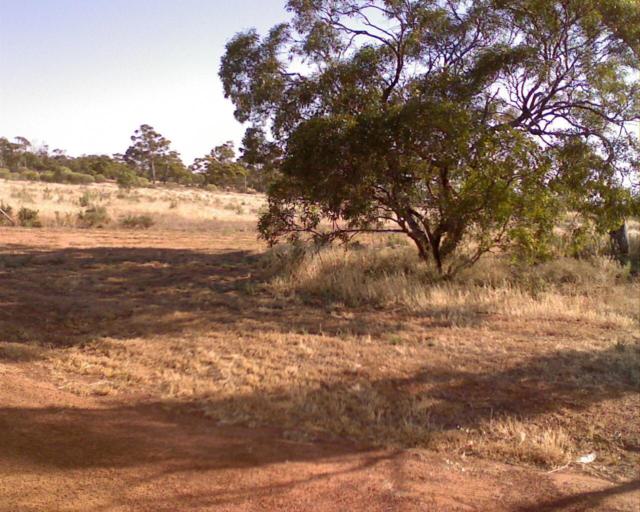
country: AU
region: Western Australia
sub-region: Merredin
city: Merredin
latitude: -31.1134
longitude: 117.7867
